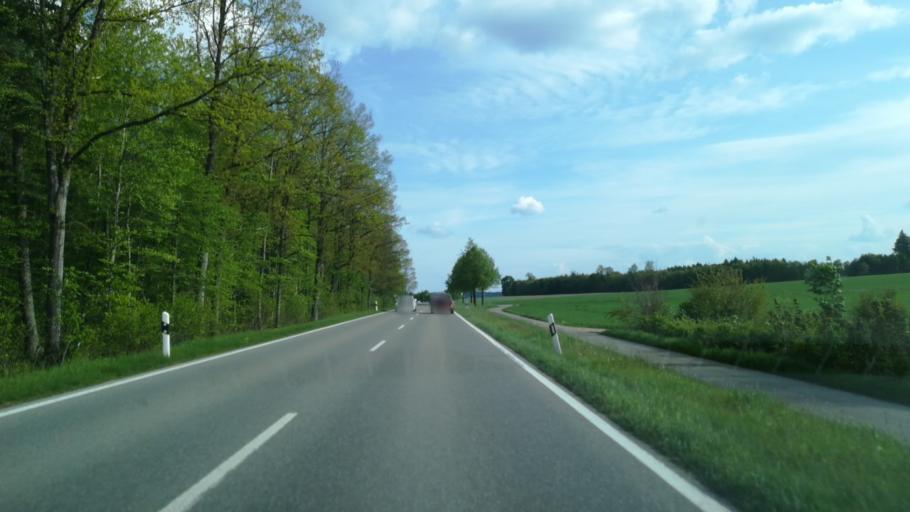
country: DE
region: Baden-Wuerttemberg
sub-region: Freiburg Region
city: Muhlingen
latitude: 47.9351
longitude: 9.0479
